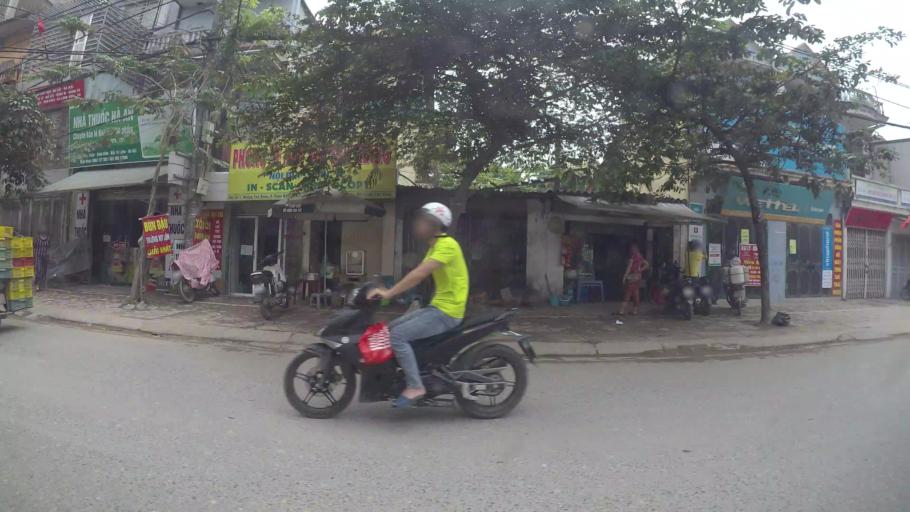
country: VN
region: Ha Noi
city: Tay Ho
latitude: 21.0797
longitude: 105.7855
